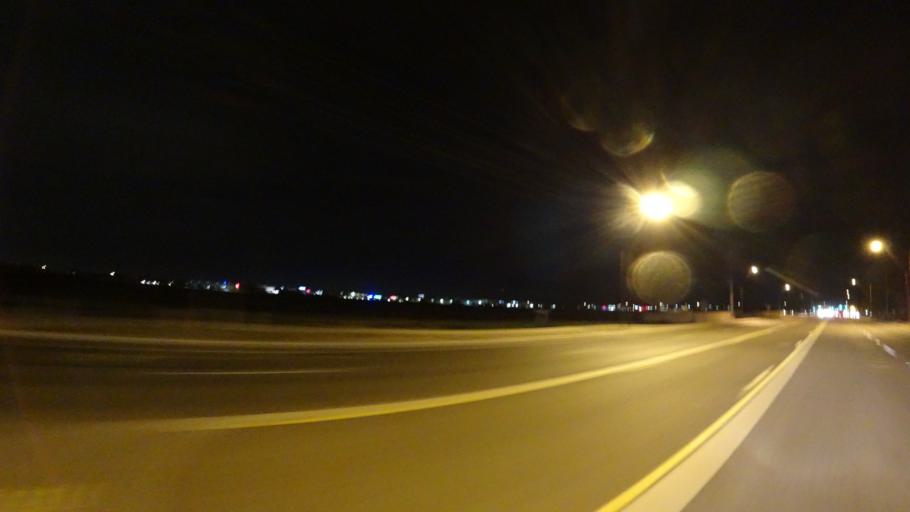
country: US
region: Arizona
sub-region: Maricopa County
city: Queen Creek
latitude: 33.2487
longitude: -111.6430
